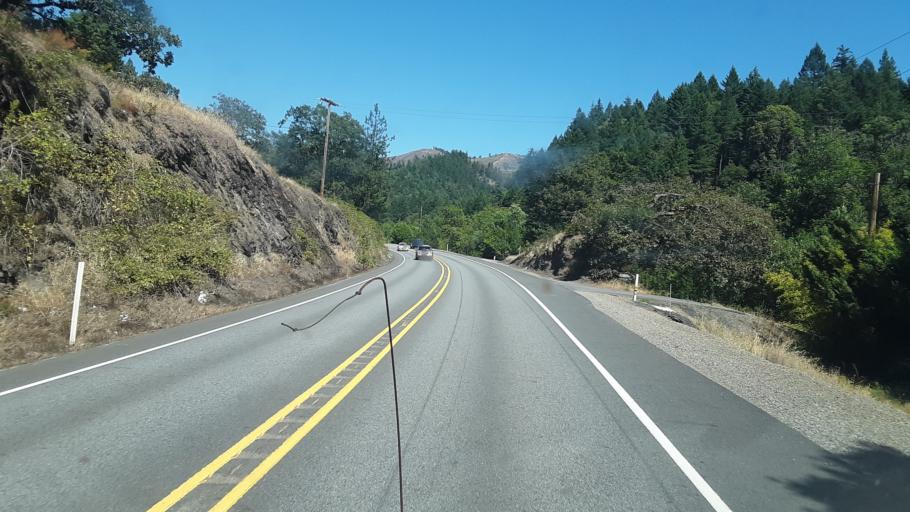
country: US
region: Oregon
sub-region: Josephine County
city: Redwood
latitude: 42.3624
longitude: -123.5194
